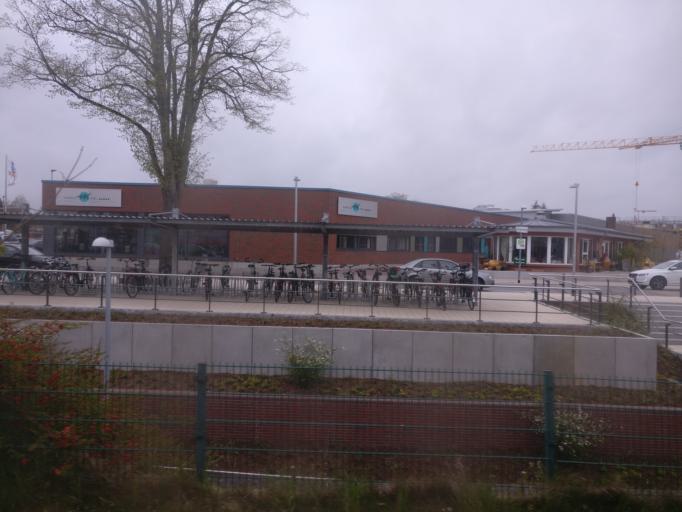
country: DE
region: Schleswig-Holstein
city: Wattenbek
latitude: 54.1741
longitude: 10.0430
